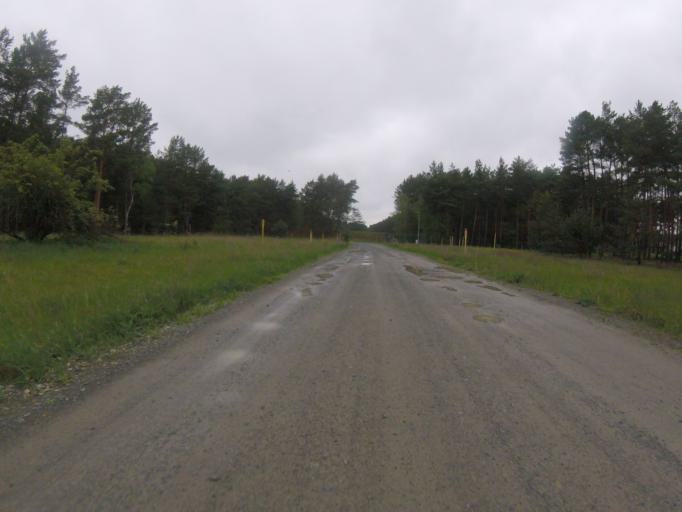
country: DE
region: Brandenburg
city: Schwerin
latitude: 52.1945
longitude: 13.6199
